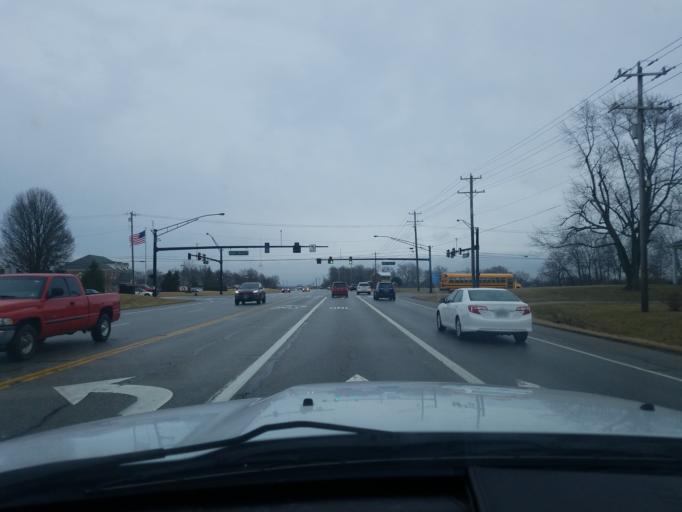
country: US
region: Ohio
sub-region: Butler County
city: Wetherington
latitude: 39.3519
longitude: -84.3484
